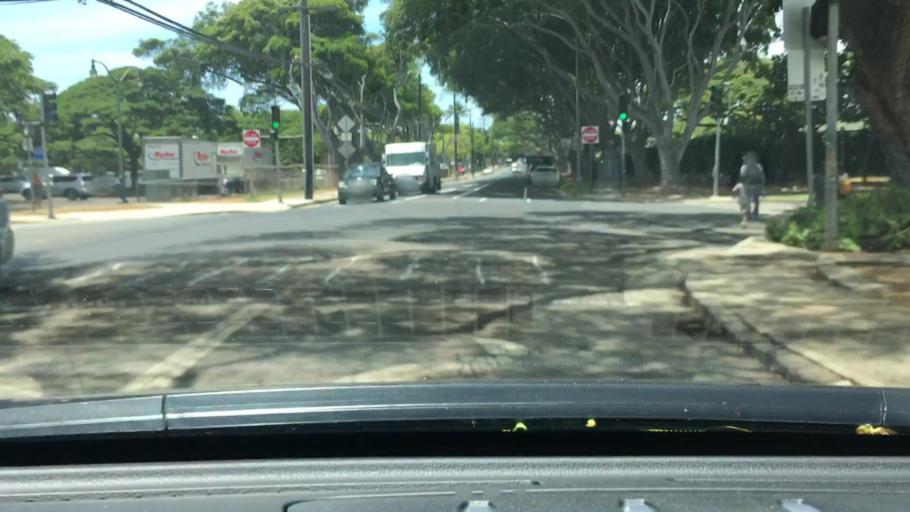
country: US
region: Hawaii
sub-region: Honolulu County
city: Honolulu
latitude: 21.2691
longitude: -157.8156
